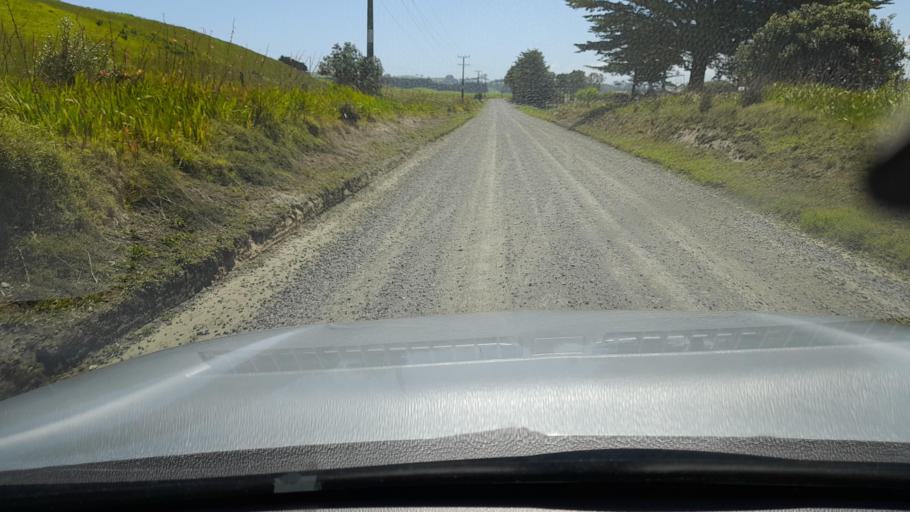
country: NZ
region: Northland
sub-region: Kaipara District
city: Dargaville
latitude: -36.0595
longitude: 173.8746
